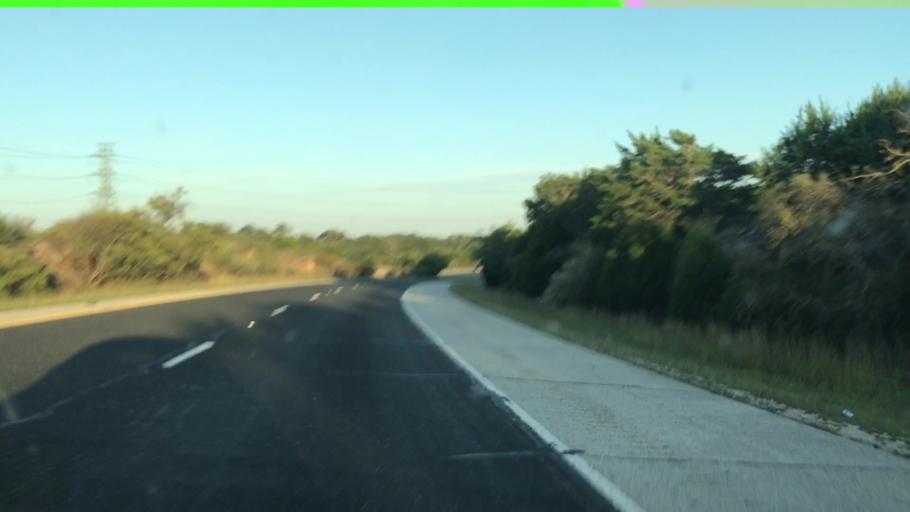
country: US
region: Texas
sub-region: Kerr County
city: Kerrville
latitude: 30.0677
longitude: -99.0583
